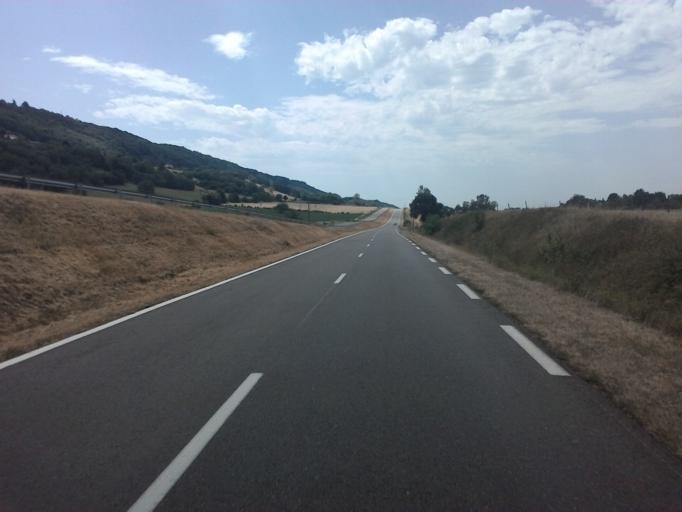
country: FR
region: Franche-Comte
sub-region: Departement du Jura
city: Saint-Amour
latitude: 46.4118
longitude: 5.3518
